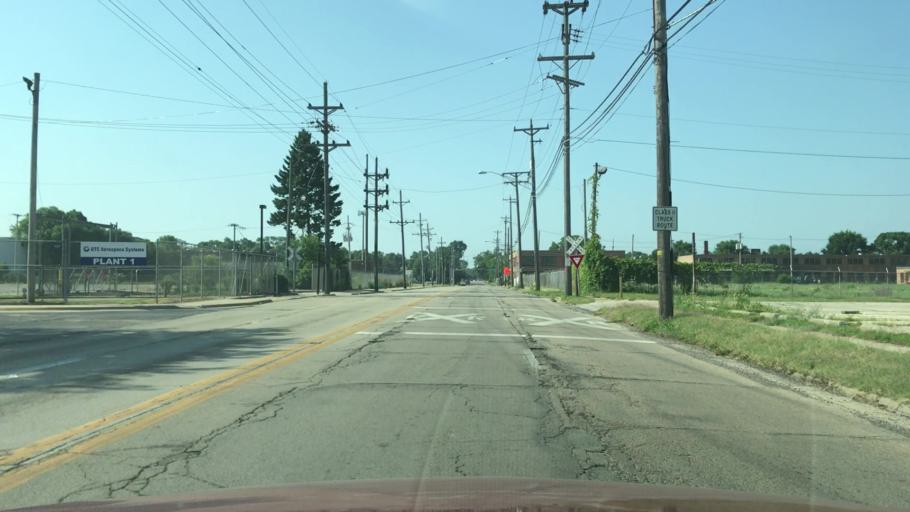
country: US
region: Illinois
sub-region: Winnebago County
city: Rockford
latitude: 42.2410
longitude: -89.0772
